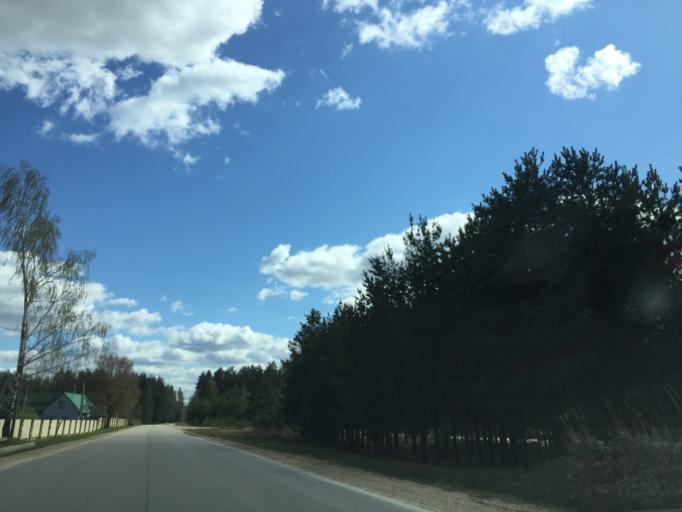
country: LV
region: Vilanu
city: Vilani
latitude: 56.5726
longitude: 27.0456
